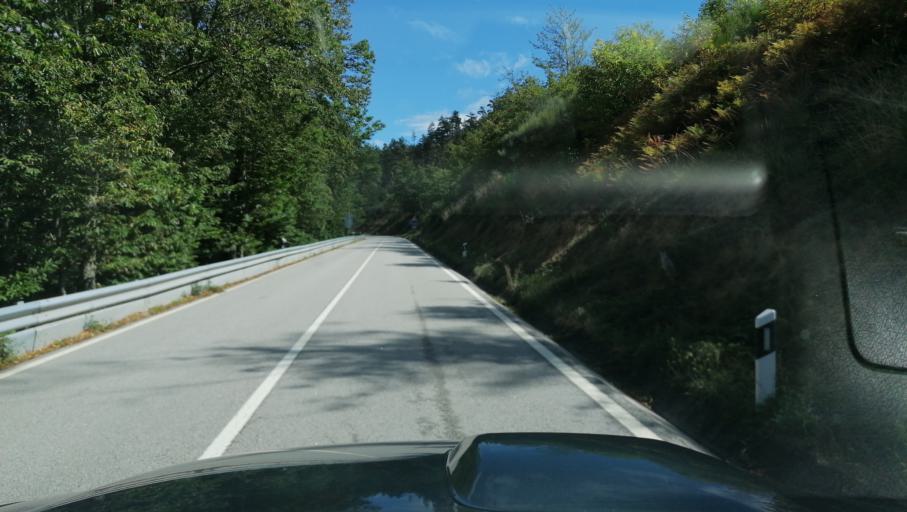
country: PT
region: Vila Real
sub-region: Vila Pouca de Aguiar
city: Vila Pouca de Aguiar
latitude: 41.5108
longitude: -7.6143
